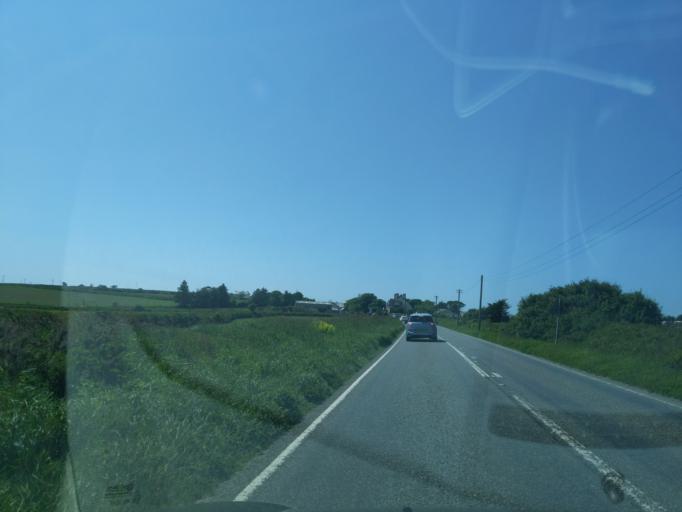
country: GB
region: England
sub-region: Cornwall
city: Jacobstow
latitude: 50.6613
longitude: -4.5700
